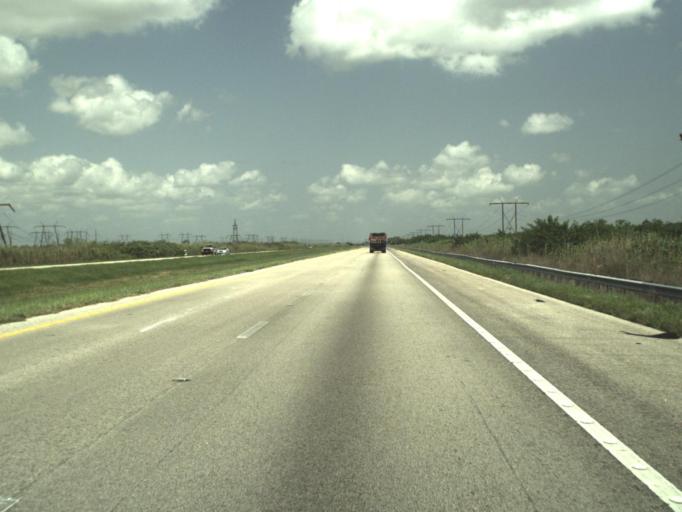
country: US
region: Florida
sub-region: Broward County
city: Weston
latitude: 26.2928
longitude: -80.5052
